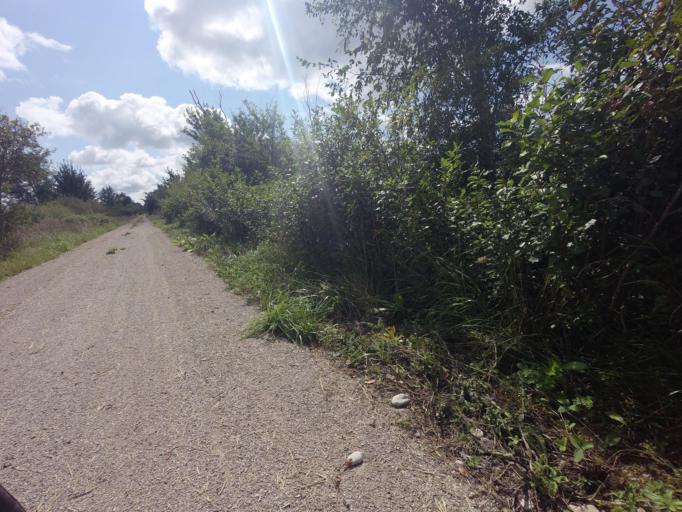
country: CA
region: Ontario
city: Huron East
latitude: 43.6513
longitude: -81.2293
